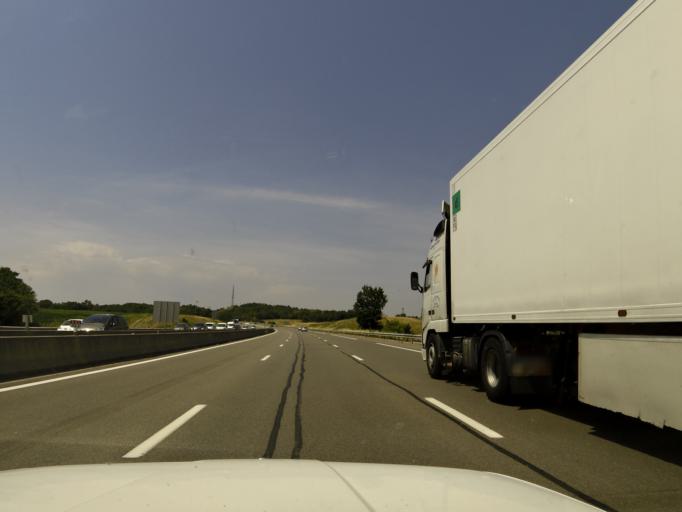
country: FR
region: Rhone-Alpes
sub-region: Departement de l'Ain
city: Beligneux
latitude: 45.8643
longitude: 5.1424
